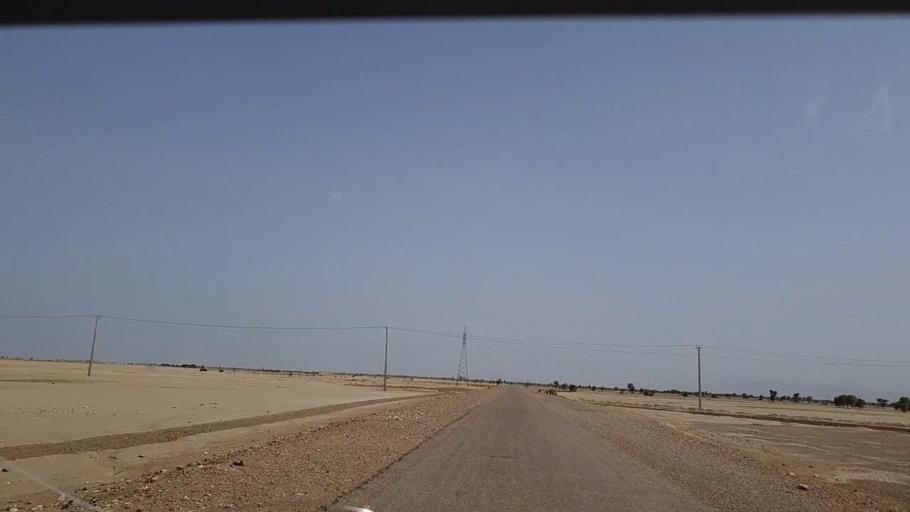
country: PK
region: Sindh
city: Johi
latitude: 26.6709
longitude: 67.5082
